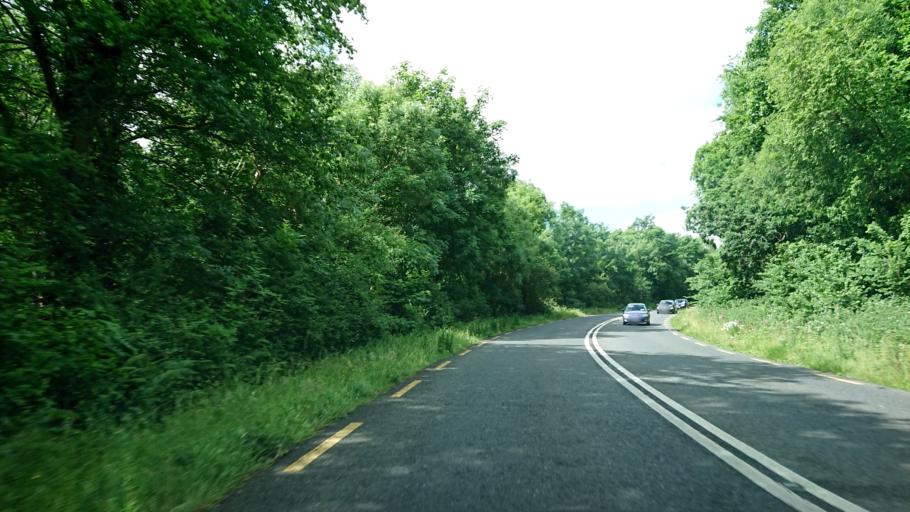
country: IE
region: Leinster
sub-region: Kilkenny
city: Mooncoin
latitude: 52.2316
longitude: -7.2178
